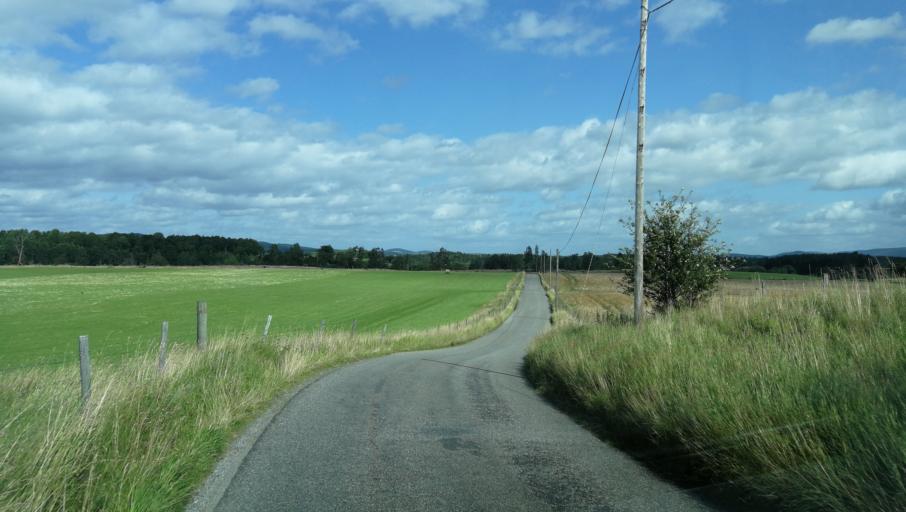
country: GB
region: Scotland
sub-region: Highland
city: Aviemore
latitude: 57.2118
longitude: -3.7727
